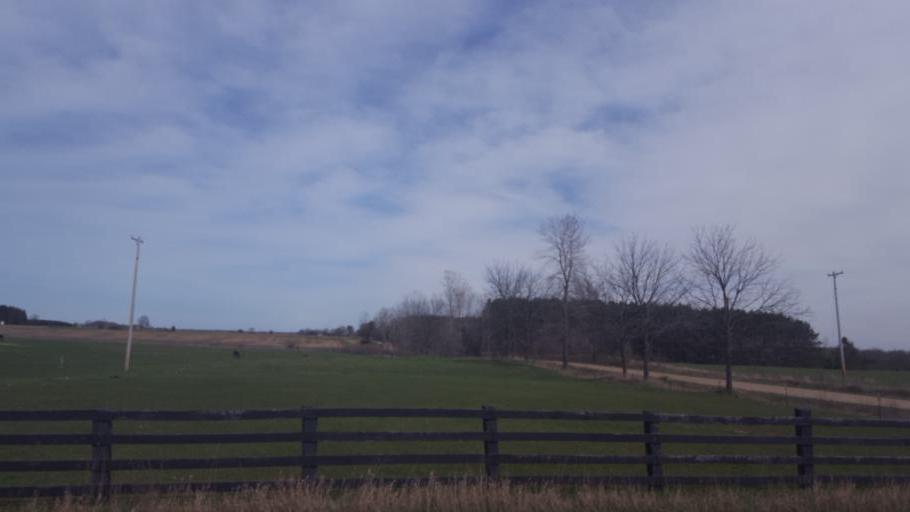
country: US
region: Michigan
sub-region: Gladwin County
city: Gladwin
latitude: 43.9527
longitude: -84.5451
